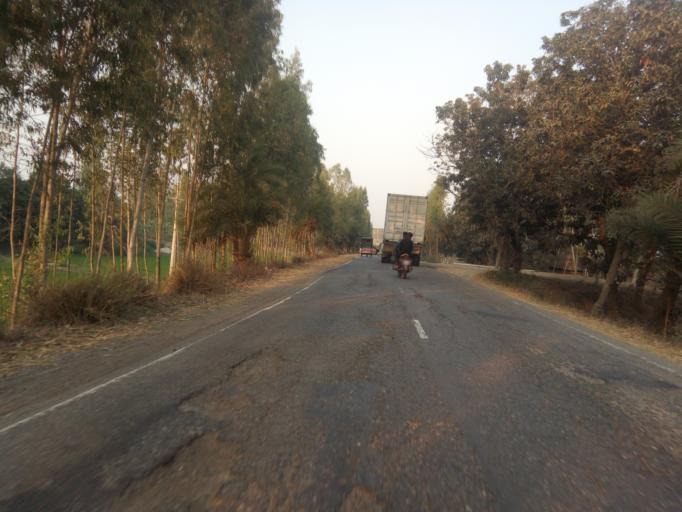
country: BD
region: Rajshahi
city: Par Naogaon
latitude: 24.5444
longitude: 89.1871
